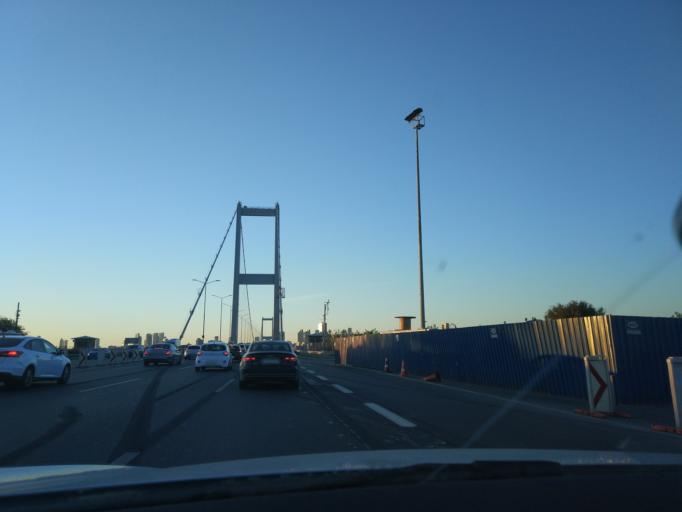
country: TR
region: Istanbul
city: UEskuedar
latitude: 41.0392
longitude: 29.0411
